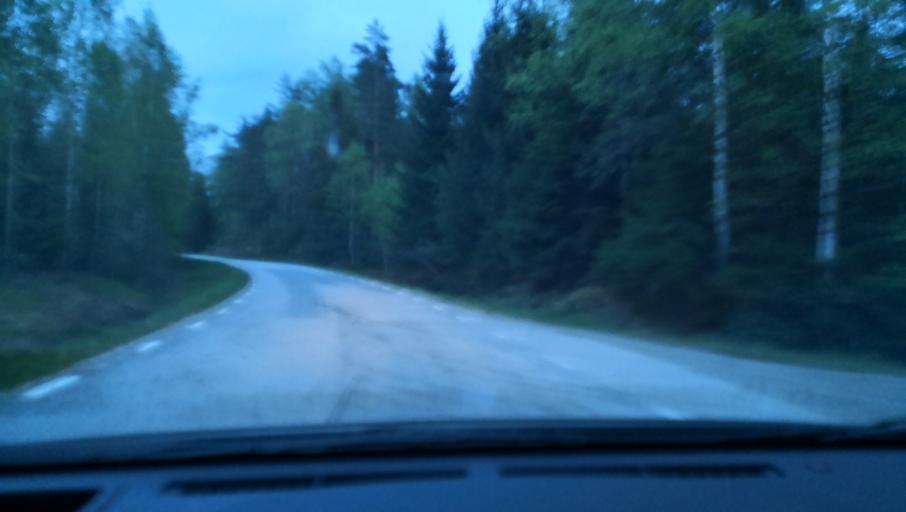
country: SE
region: Vaestmanland
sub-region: Skinnskattebergs Kommun
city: Skinnskatteberg
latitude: 59.6766
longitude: 15.6052
